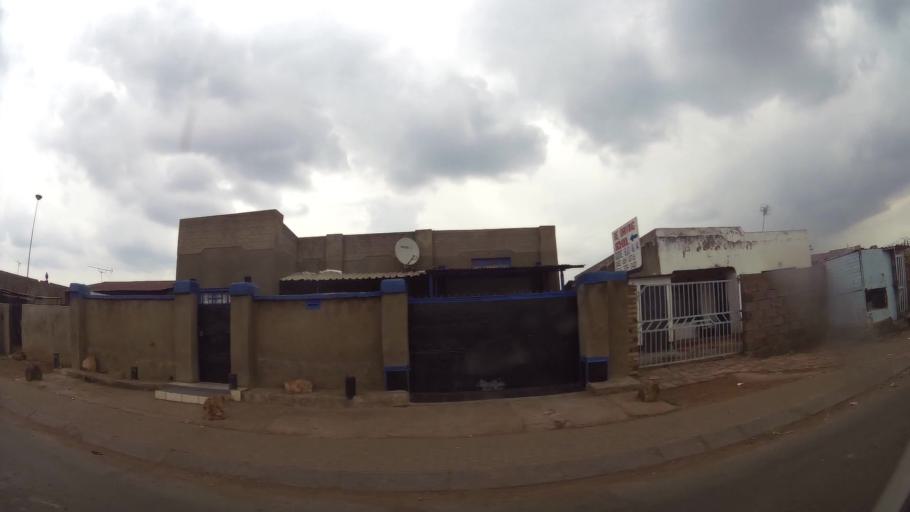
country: ZA
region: Gauteng
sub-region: Ekurhuleni Metropolitan Municipality
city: Germiston
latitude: -26.3477
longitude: 28.1498
